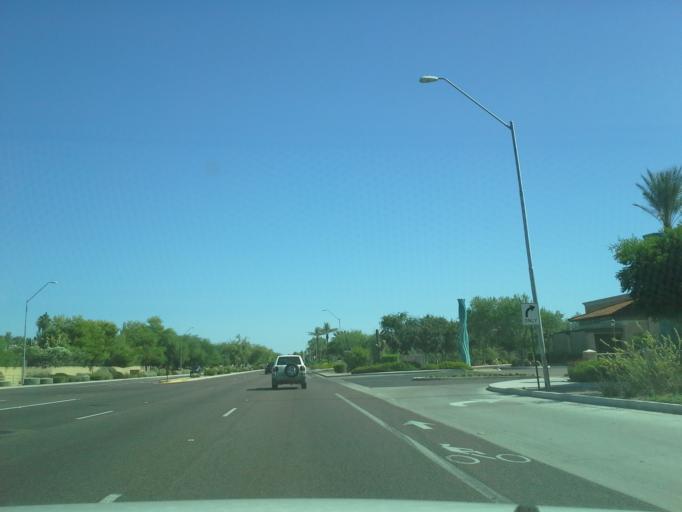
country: US
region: Arizona
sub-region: Maricopa County
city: Paradise Valley
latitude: 33.5418
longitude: -111.9256
